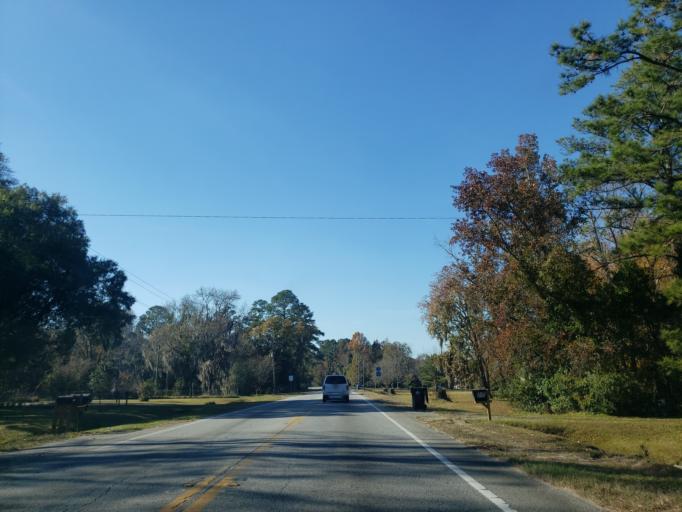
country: US
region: Georgia
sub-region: Glynn County
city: Dock Junction
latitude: 31.2732
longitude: -81.5648
